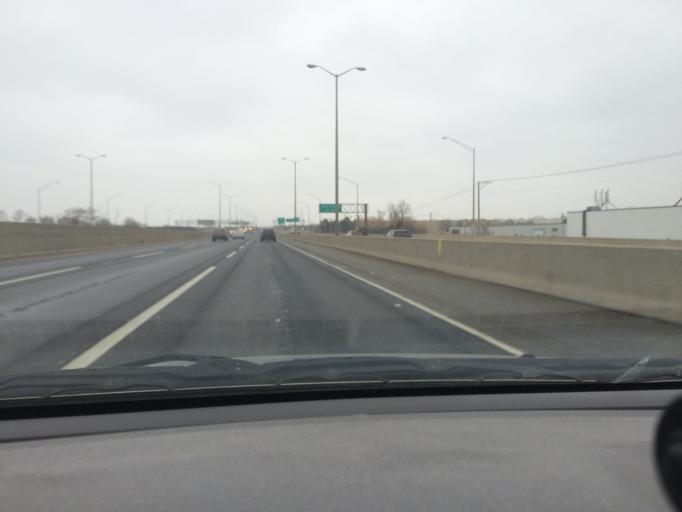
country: US
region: Illinois
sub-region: DuPage County
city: Glendale Heights
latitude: 41.9234
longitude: -88.0378
